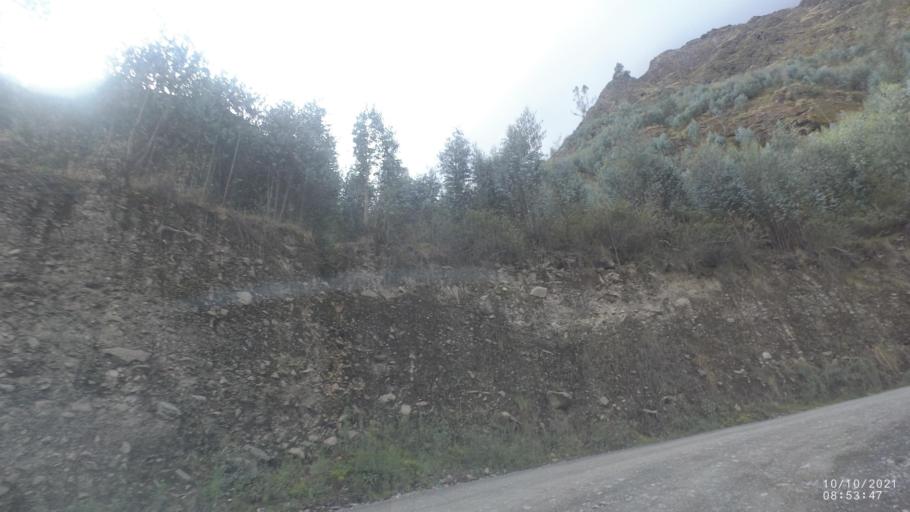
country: BO
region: La Paz
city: Quime
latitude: -16.9875
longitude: -67.2303
